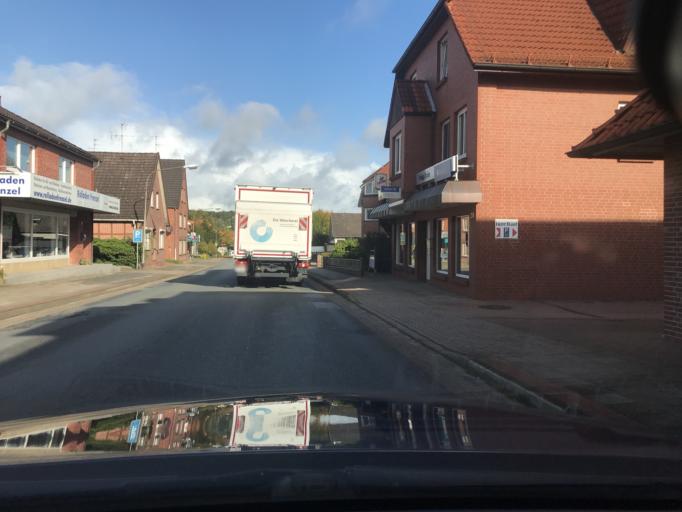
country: DE
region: Lower Saxony
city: Harsefeld
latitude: 53.4548
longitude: 9.4996
